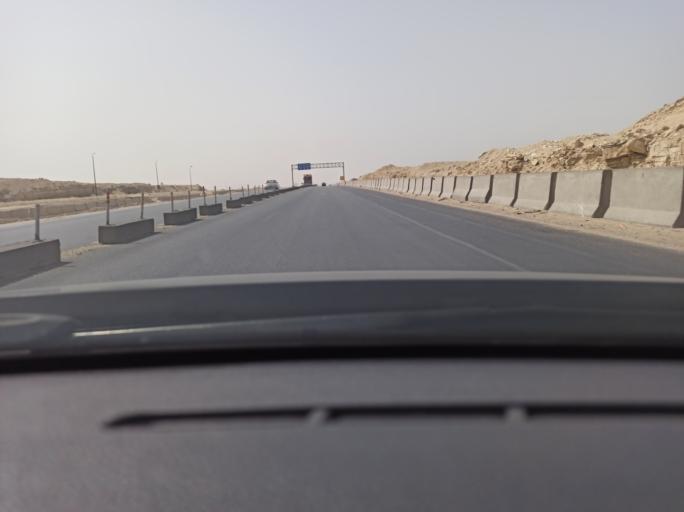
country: EG
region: Muhafazat al Fayyum
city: Al Wasitah
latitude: 29.2929
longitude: 31.2749
